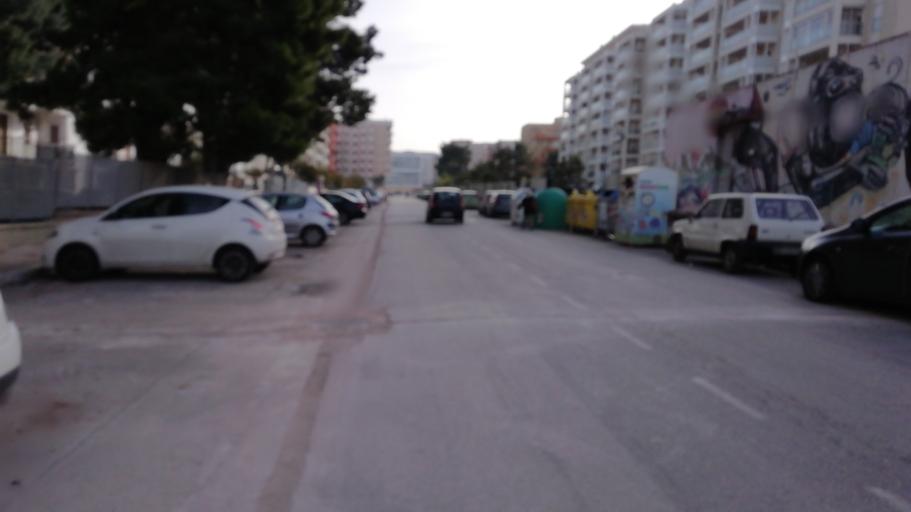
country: IT
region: Apulia
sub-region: Provincia di Bari
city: Triggiano
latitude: 41.1060
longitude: 16.9148
